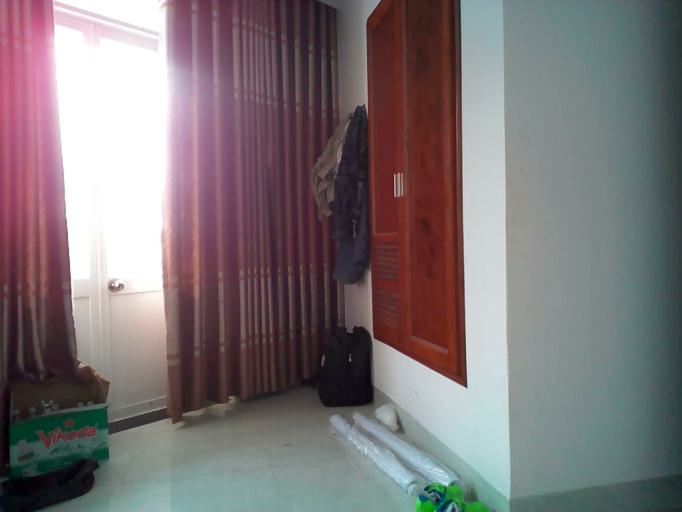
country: VN
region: Khanh Hoa
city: Nha Trang
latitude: 12.2880
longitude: 109.1956
